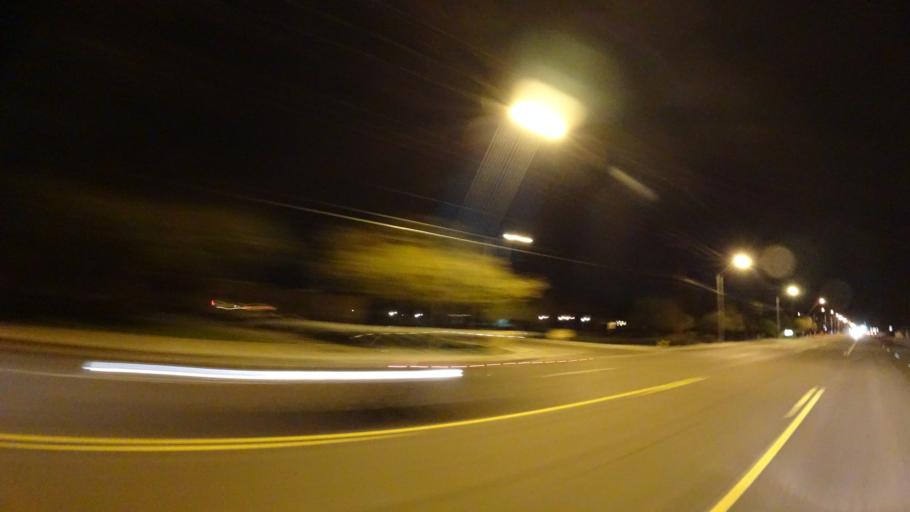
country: US
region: Arizona
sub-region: Maricopa County
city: Mesa
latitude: 33.4372
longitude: -111.7816
